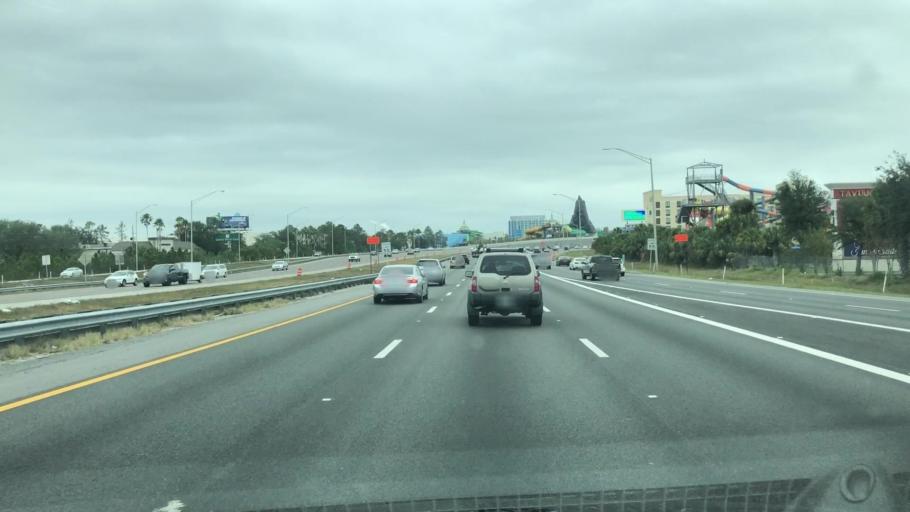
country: US
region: Florida
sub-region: Orange County
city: Doctor Phillips
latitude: 28.4528
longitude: -81.4739
